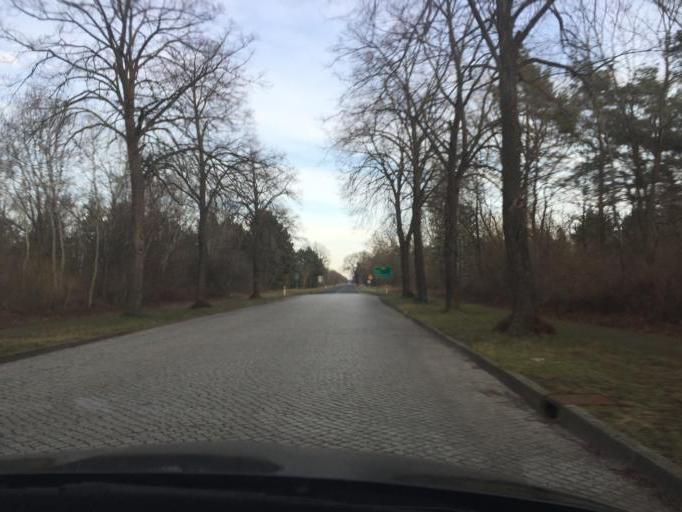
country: DE
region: Brandenburg
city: Forst
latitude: 51.7460
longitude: 14.6744
